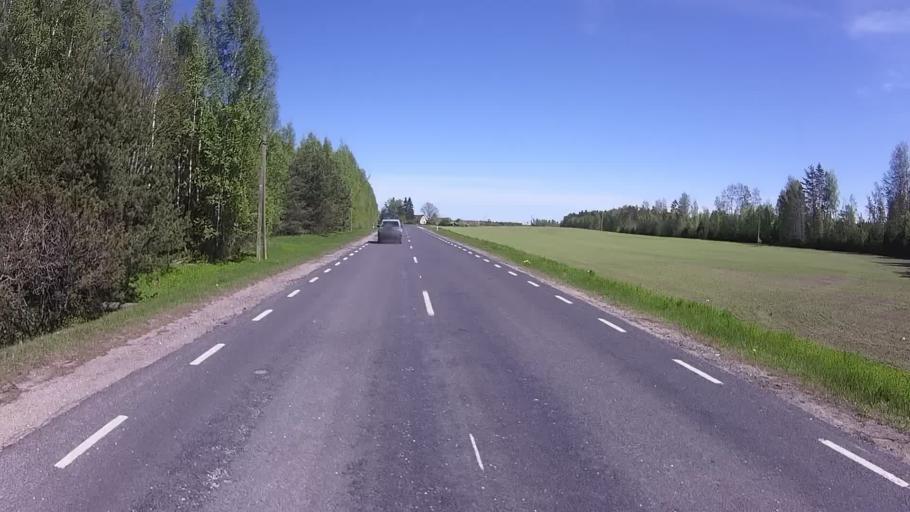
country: EE
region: Polvamaa
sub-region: Raepina vald
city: Rapina
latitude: 58.0306
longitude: 27.3862
